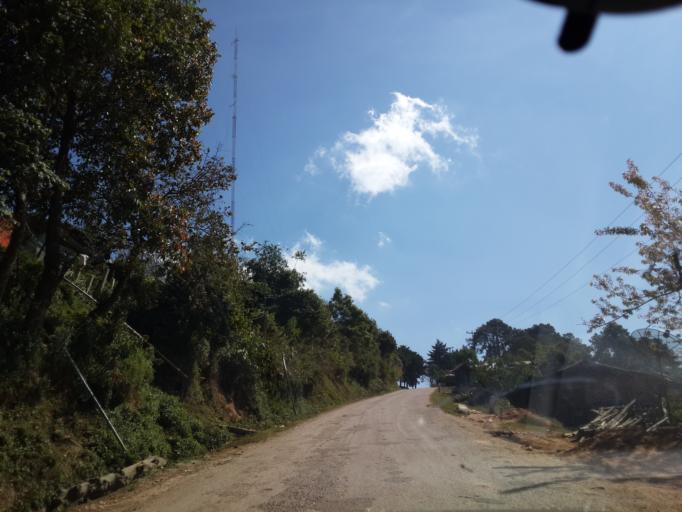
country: TH
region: Chiang Mai
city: Fang
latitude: 19.9357
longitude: 99.0418
